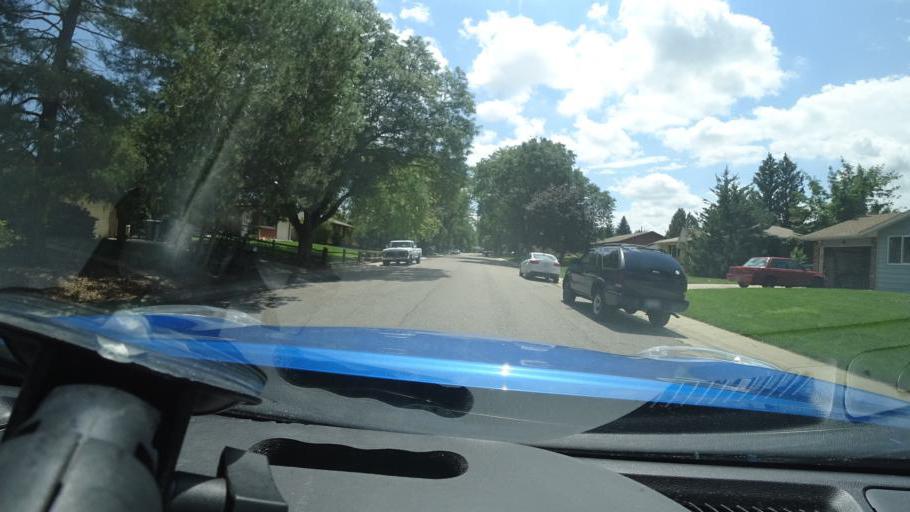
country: US
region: Colorado
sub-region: Adams County
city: Aurora
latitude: 39.7056
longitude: -104.8452
